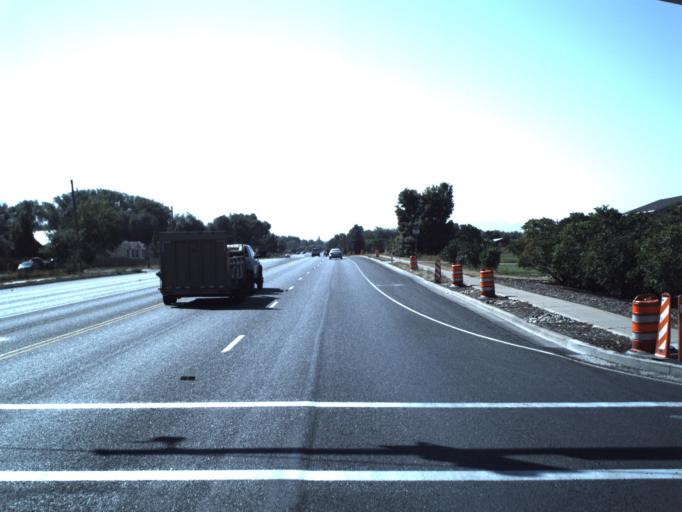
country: US
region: Utah
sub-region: Cache County
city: Nibley
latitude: 41.6855
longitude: -111.8340
